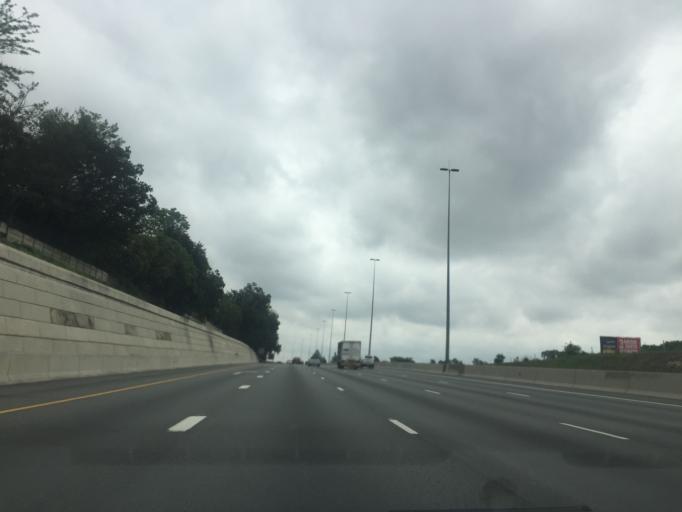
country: ZA
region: Gauteng
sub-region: City of Johannesburg Metropolitan Municipality
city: Midrand
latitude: -26.0354
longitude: 28.0402
